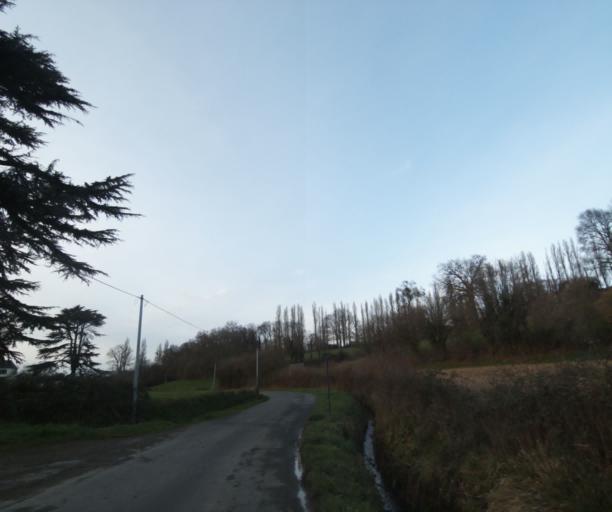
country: FR
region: Pays de la Loire
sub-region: Departement de la Sarthe
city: Allonnes
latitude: 47.9935
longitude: 0.1654
